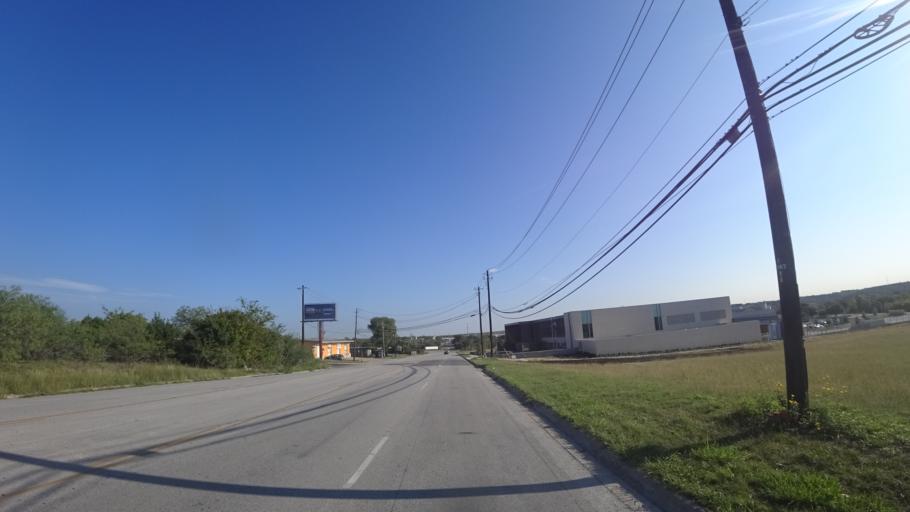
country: US
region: Texas
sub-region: Travis County
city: Austin
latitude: 30.3206
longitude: -97.6600
